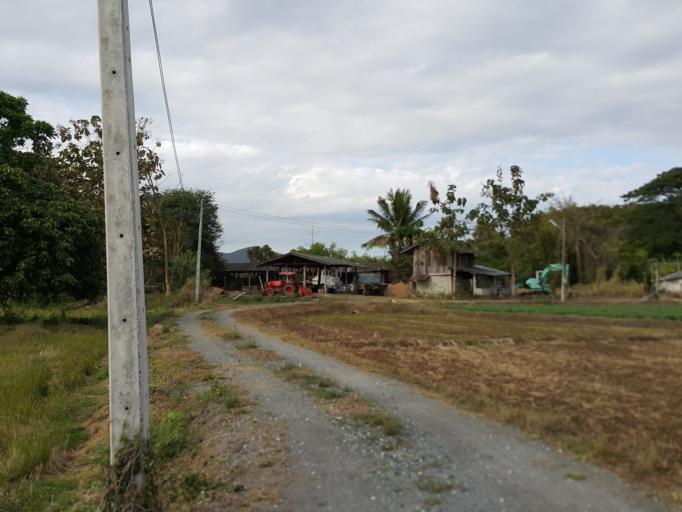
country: TH
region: Chiang Mai
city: San Sai
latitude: 18.8787
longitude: 99.1100
